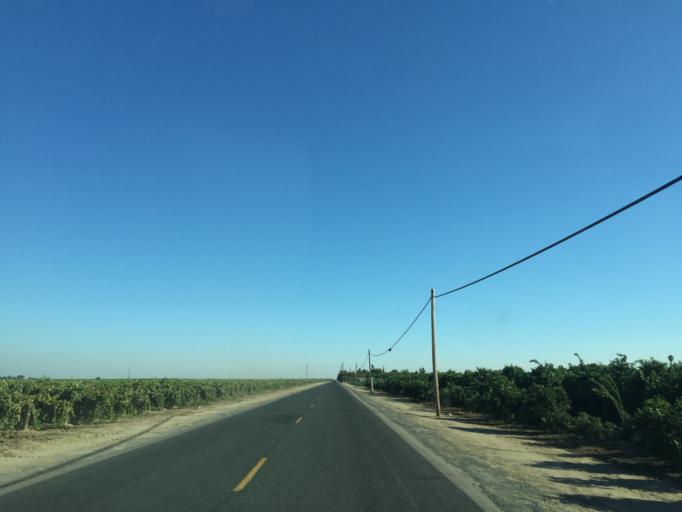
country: US
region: California
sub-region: Tulare County
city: London
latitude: 36.4845
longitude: -119.4385
